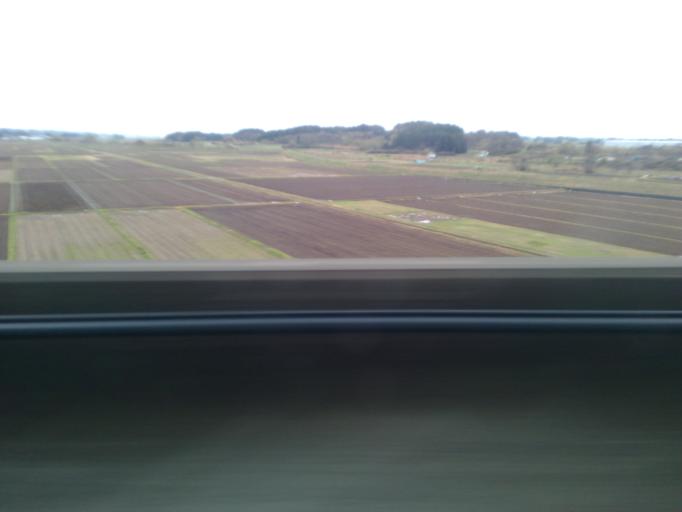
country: JP
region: Miyagi
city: Furukawa
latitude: 38.6500
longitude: 141.0157
